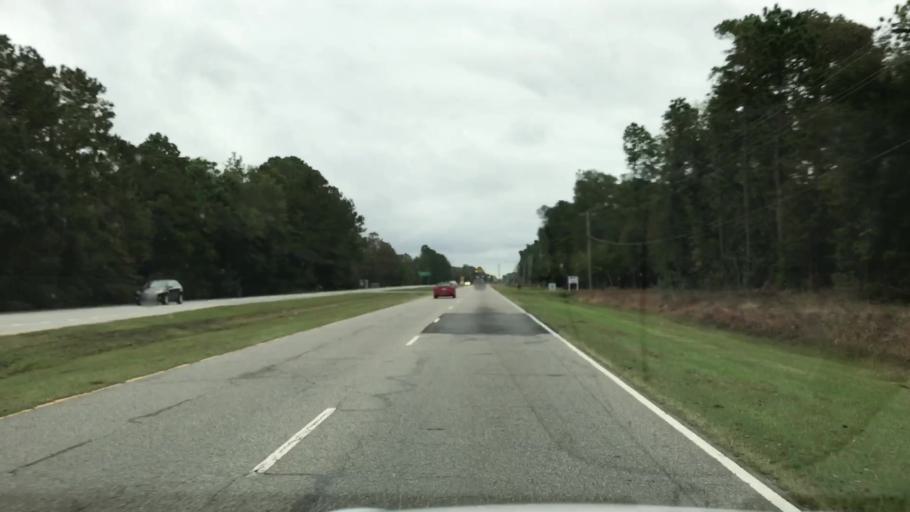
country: US
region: South Carolina
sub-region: Georgetown County
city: Georgetown
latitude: 33.3221
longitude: -79.3206
